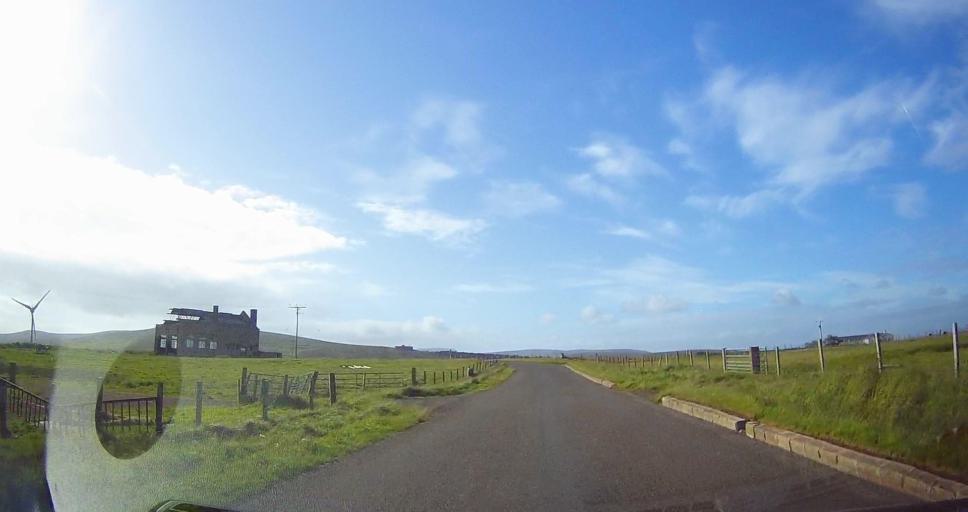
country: GB
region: Scotland
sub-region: Orkney Islands
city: Stromness
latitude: 58.8219
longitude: -3.2057
